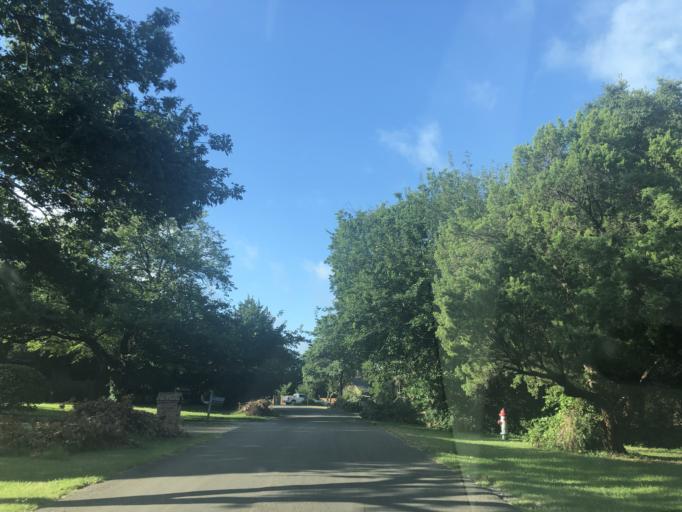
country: US
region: Texas
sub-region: Dallas County
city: Duncanville
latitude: 32.6709
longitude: -96.9209
